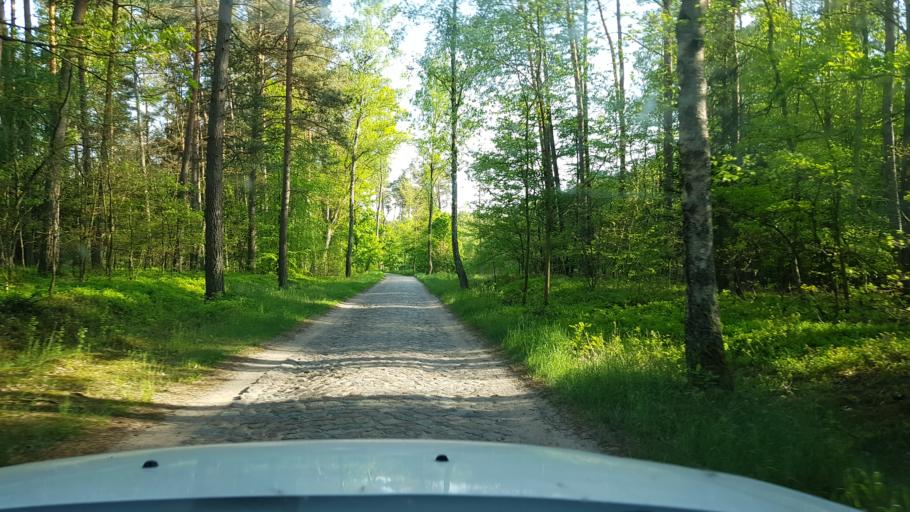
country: PL
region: West Pomeranian Voivodeship
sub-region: Powiat lobeski
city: Resko
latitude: 53.7282
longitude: 15.3255
